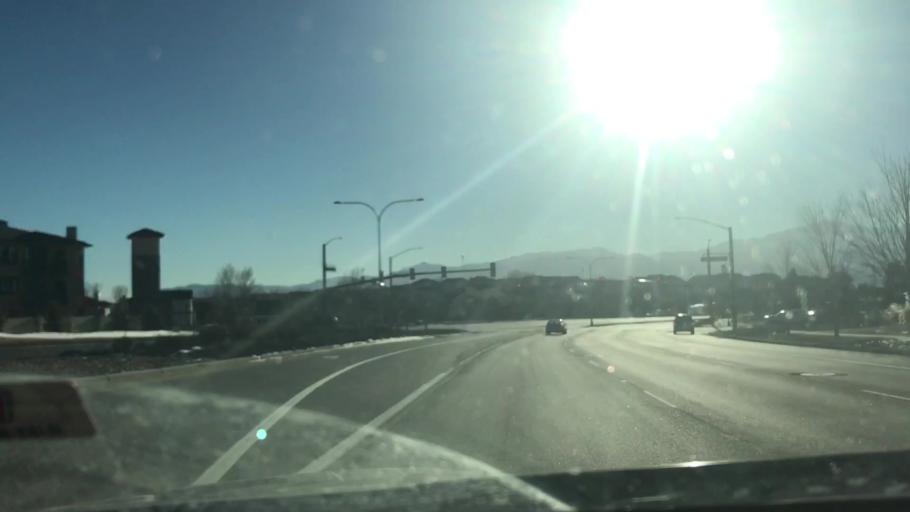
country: US
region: Colorado
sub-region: El Paso County
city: Black Forest
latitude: 38.9671
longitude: -104.7451
